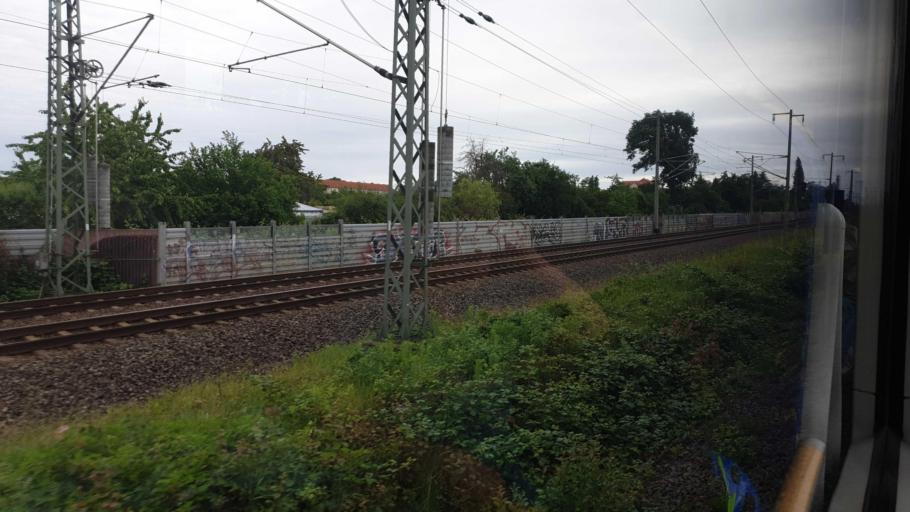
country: DE
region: Saxony
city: Taucha
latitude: 51.3442
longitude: 12.4382
